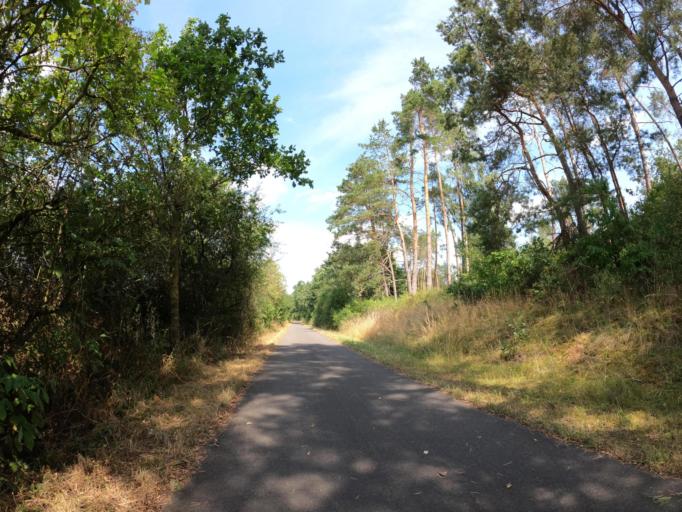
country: DE
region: Mecklenburg-Vorpommern
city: Woldegk
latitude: 53.3106
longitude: 13.5753
